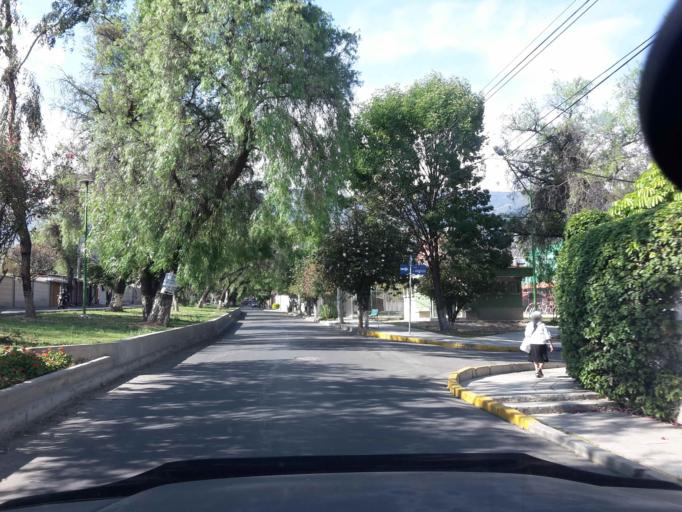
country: BO
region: Cochabamba
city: Cochabamba
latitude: -17.3746
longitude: -66.1726
